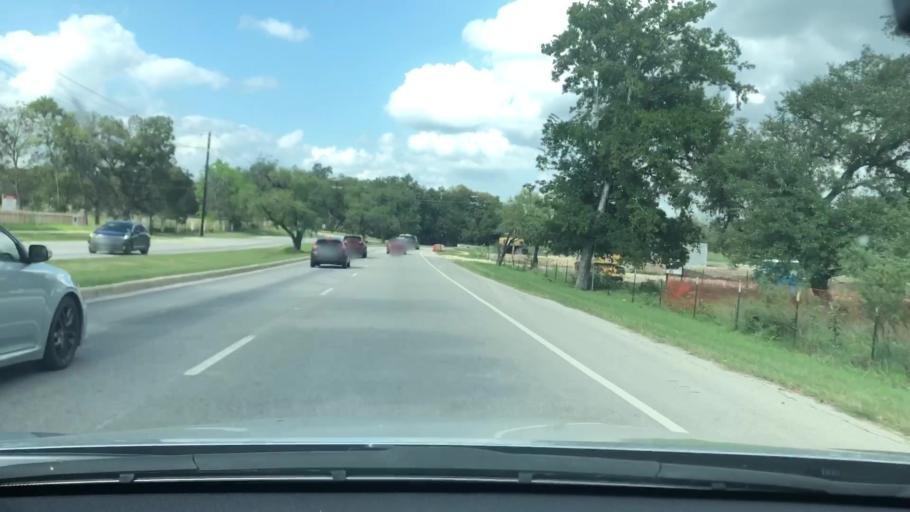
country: US
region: Texas
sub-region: Kendall County
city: Boerne
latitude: 29.7855
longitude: -98.7176
